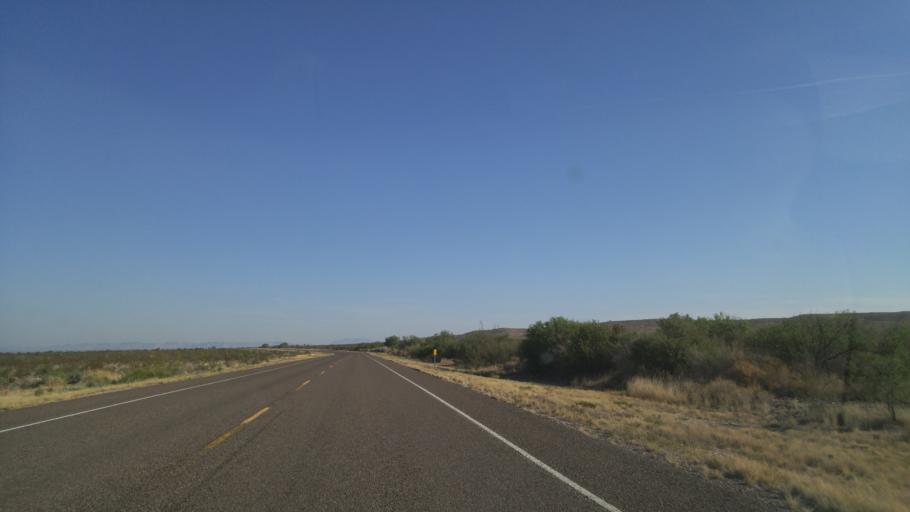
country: US
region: Texas
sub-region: Brewster County
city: Alpine
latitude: 29.7546
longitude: -103.5692
